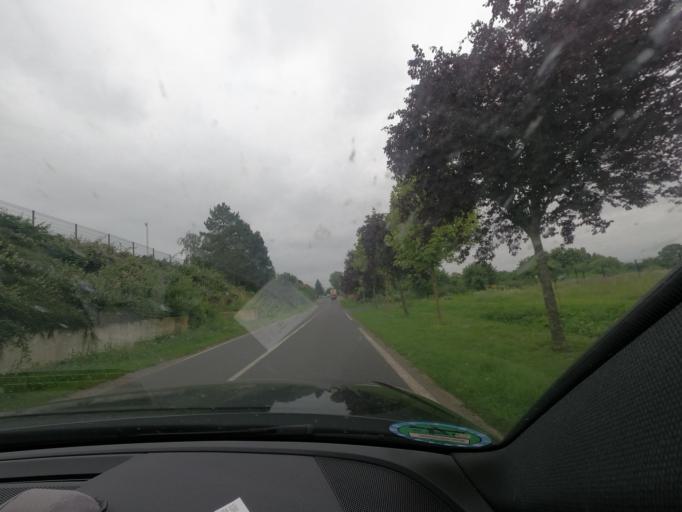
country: FR
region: Picardie
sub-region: Departement de l'Oise
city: Ressons-sur-Matz
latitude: 49.5395
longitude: 2.7360
